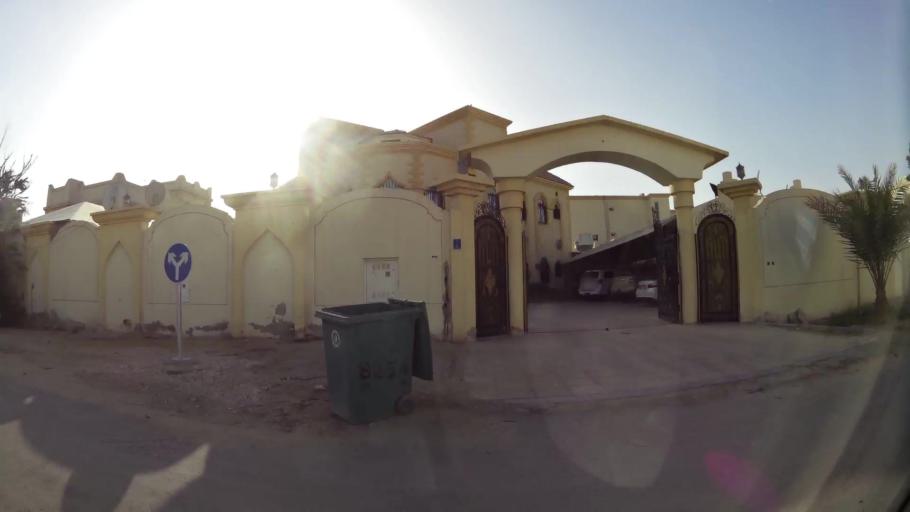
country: QA
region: Baladiyat ar Rayyan
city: Ar Rayyan
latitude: 25.3350
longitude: 51.4335
